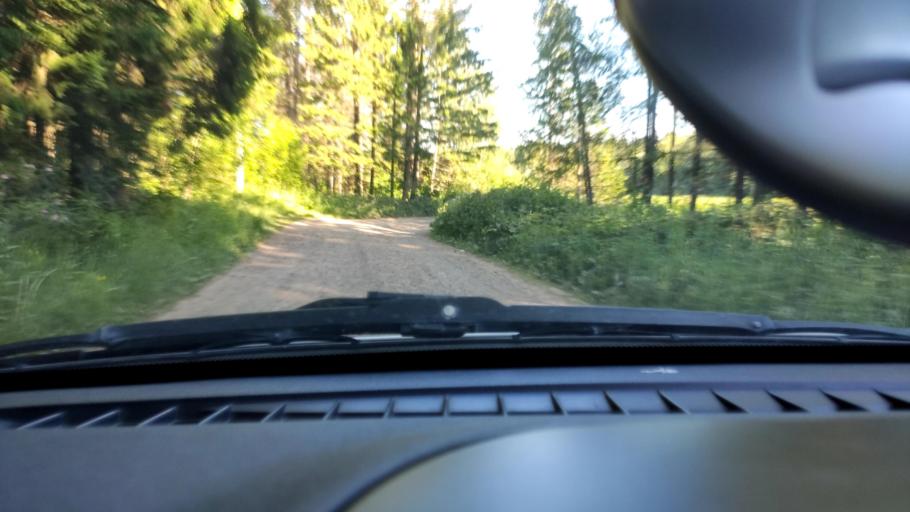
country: RU
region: Perm
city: Bershet'
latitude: 57.6984
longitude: 56.4074
